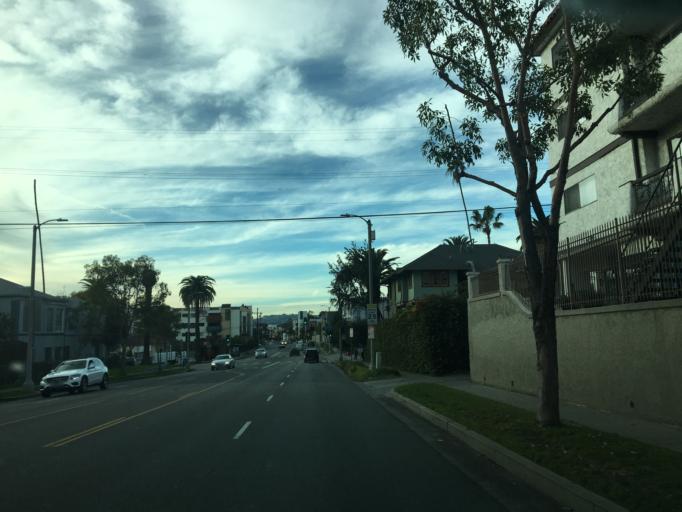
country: US
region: California
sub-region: Los Angeles County
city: Silver Lake
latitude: 34.0674
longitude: -118.2812
